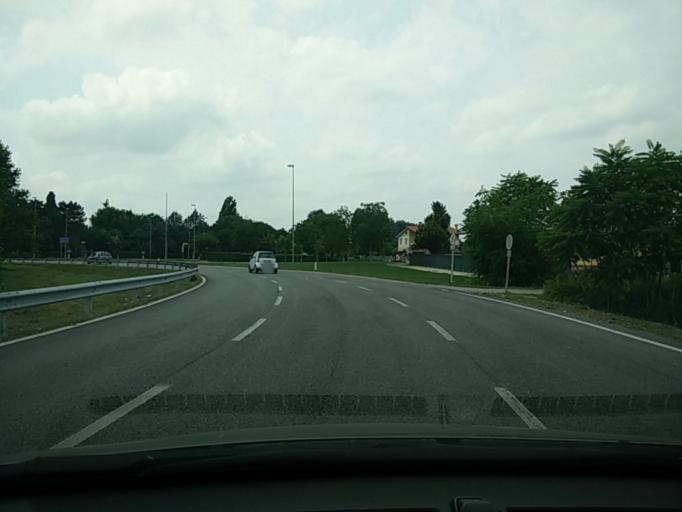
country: IT
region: Veneto
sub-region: Provincia di Venezia
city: Summaga
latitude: 45.7801
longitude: 12.8132
